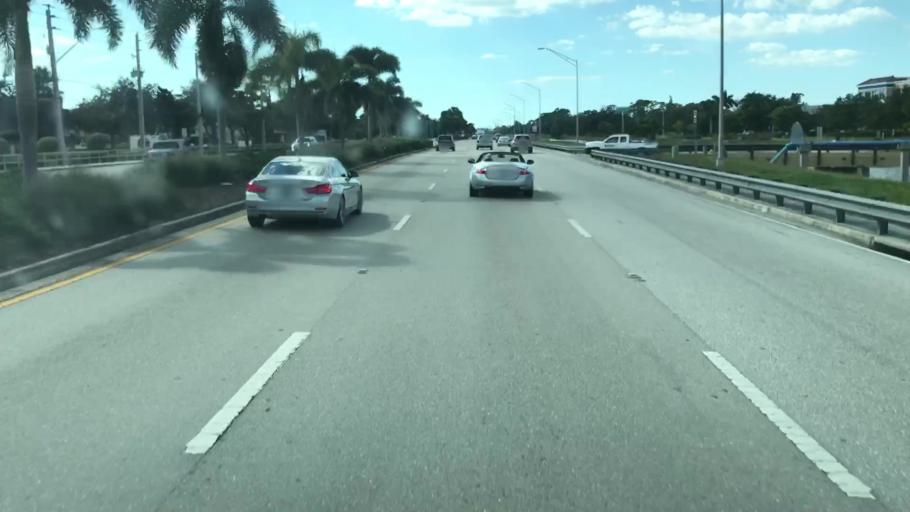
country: US
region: Florida
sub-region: Collier County
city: Naples Park
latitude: 26.2725
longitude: -81.7708
